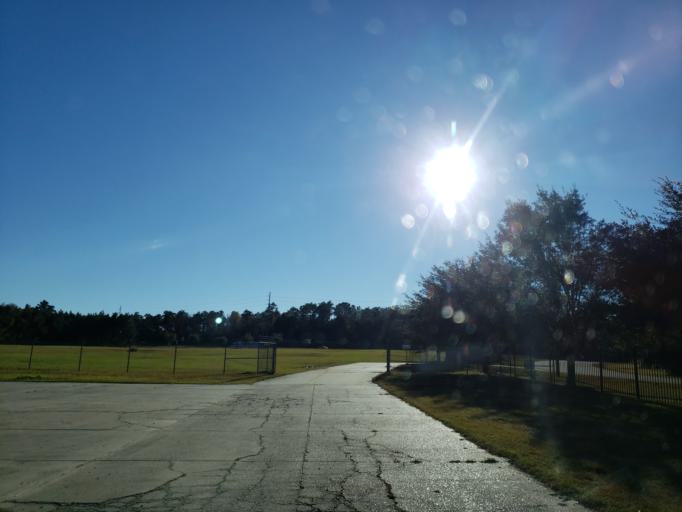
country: US
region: Mississippi
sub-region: Forrest County
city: Hattiesburg
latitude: 31.2564
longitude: -89.2783
